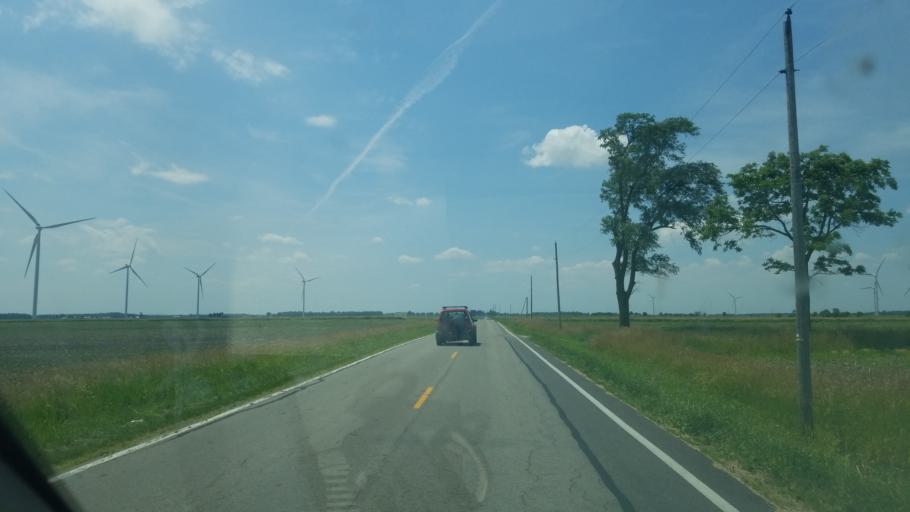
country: US
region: Ohio
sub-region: Hardin County
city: Ada
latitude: 40.7763
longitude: -83.7161
